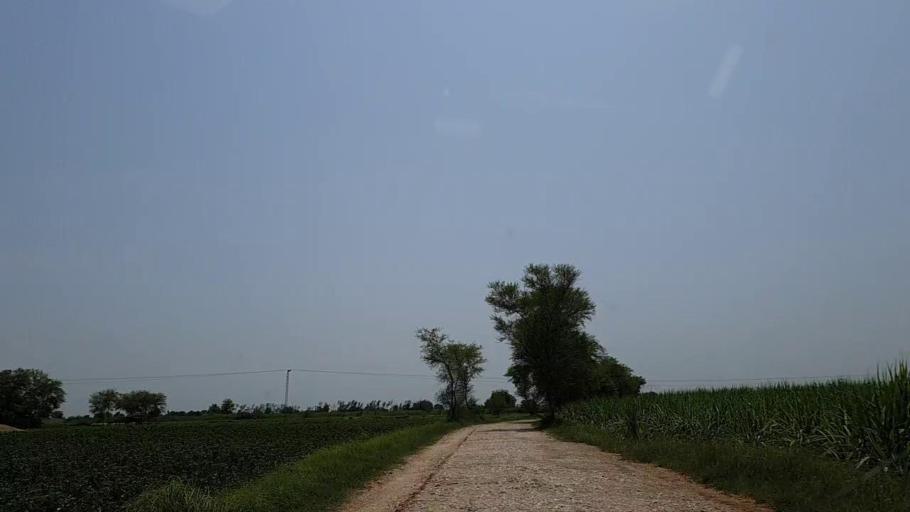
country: PK
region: Sindh
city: Ghotki
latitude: 27.9755
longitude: 69.4006
